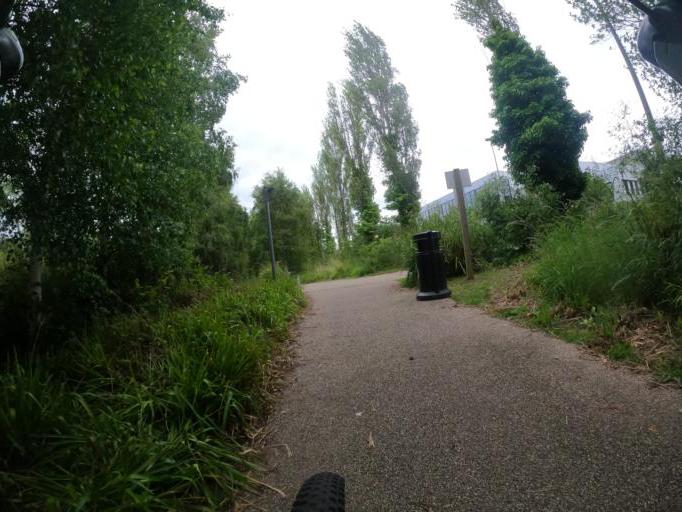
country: GB
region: Scotland
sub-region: Edinburgh
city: Edinburgh
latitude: 55.9782
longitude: -3.2467
